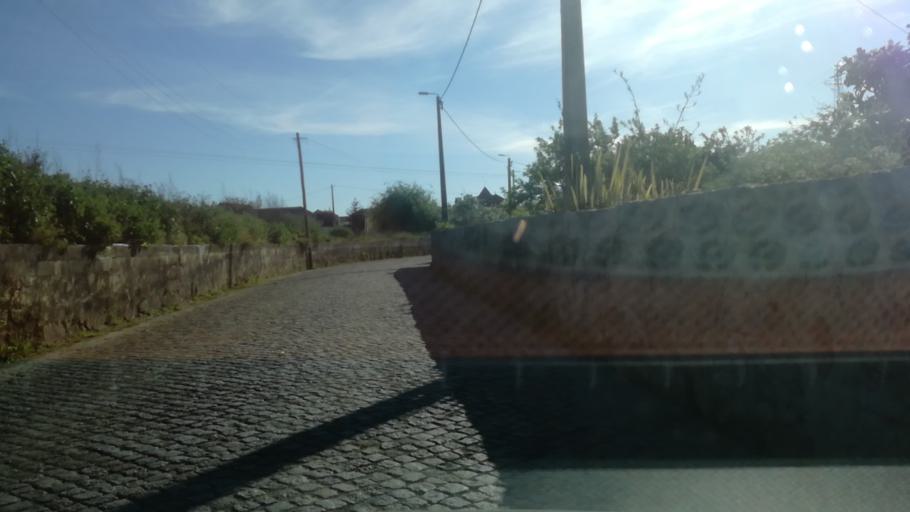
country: PT
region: Porto
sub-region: Matosinhos
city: Santa Cruz do Bispo
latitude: 41.2509
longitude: -8.6694
